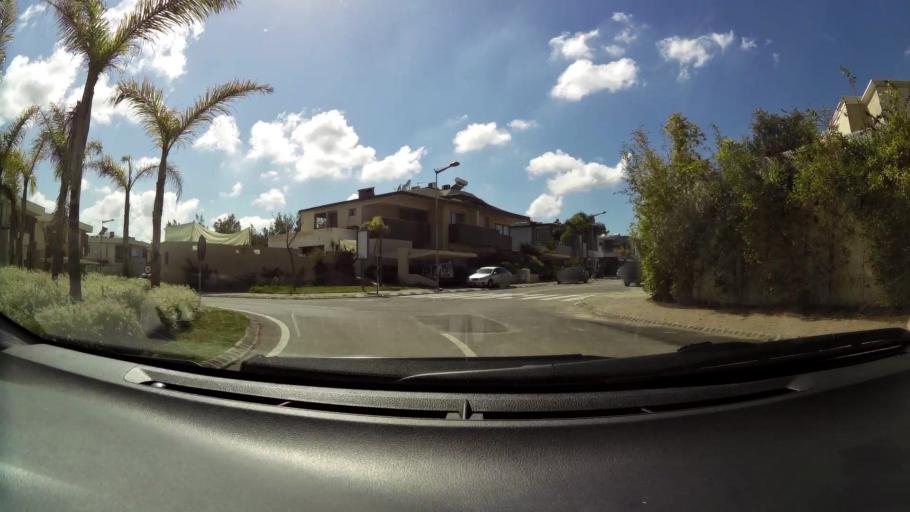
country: MA
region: Grand Casablanca
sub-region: Nouaceur
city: Bouskoura
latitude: 33.4648
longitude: -7.5979
